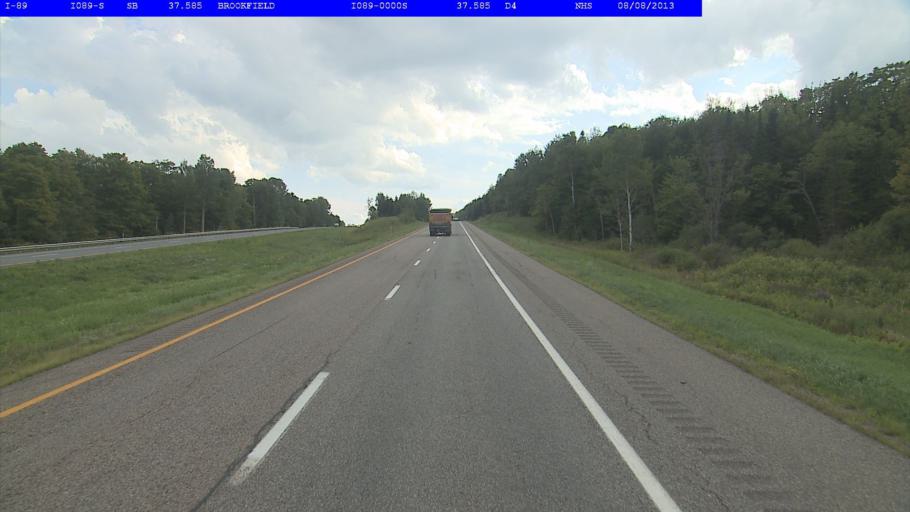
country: US
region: Vermont
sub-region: Orange County
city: Williamstown
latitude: 44.0403
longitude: -72.6115
